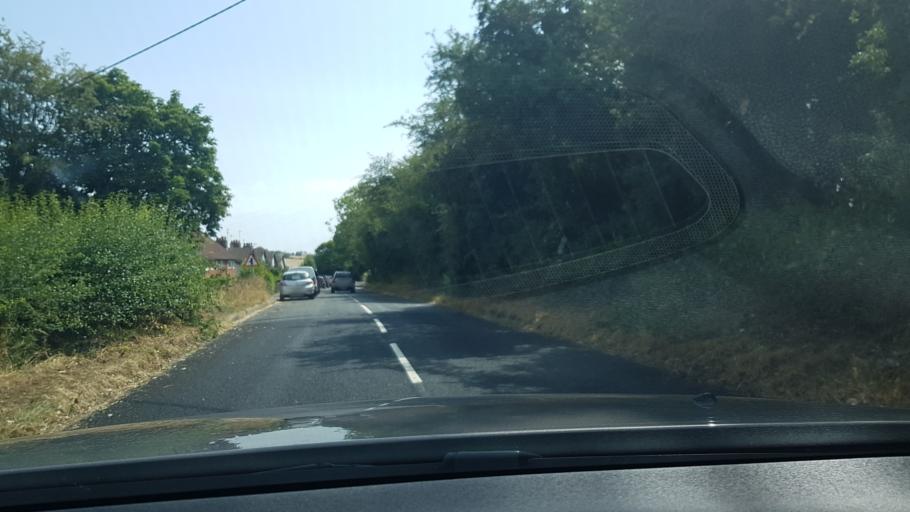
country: GB
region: England
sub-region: West Berkshire
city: Lambourn
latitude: 51.4882
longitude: -1.4807
